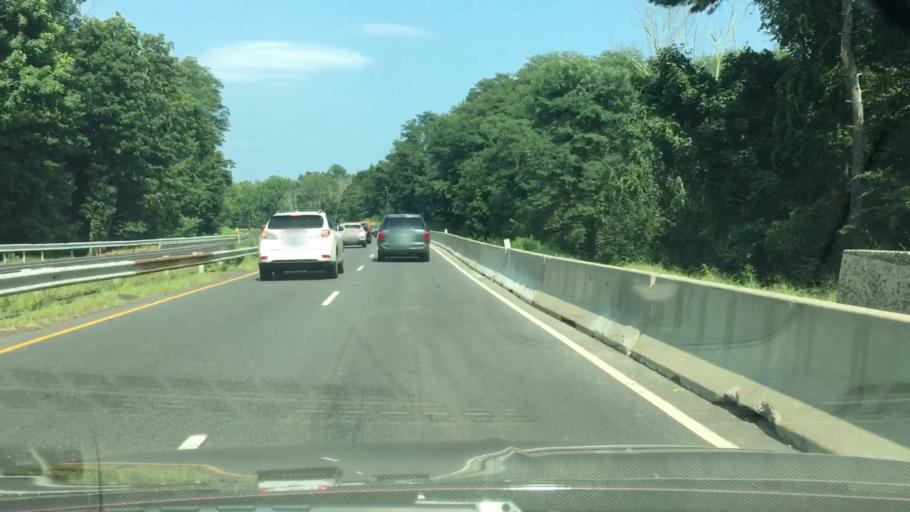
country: US
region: Connecticut
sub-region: Fairfield County
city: Westport
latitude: 41.1741
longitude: -73.3218
